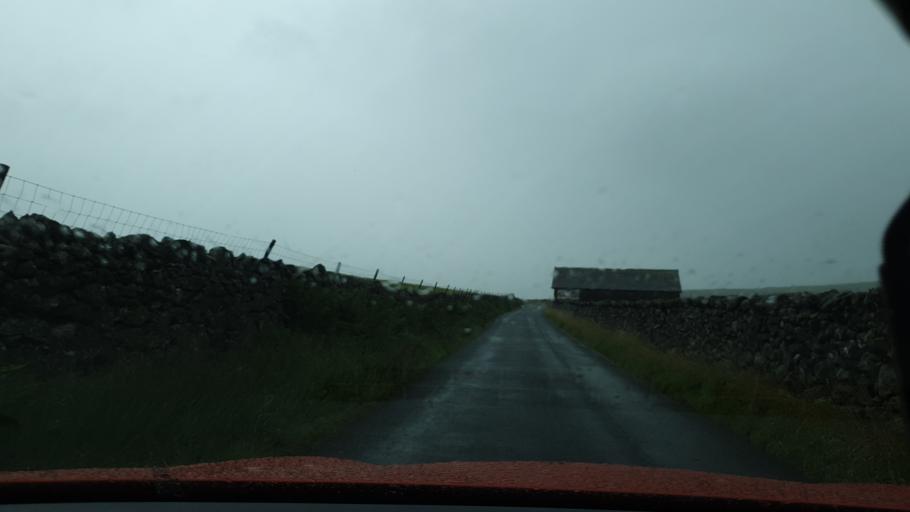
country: GB
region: England
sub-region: Cumbria
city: Millom
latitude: 54.3396
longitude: -3.2448
